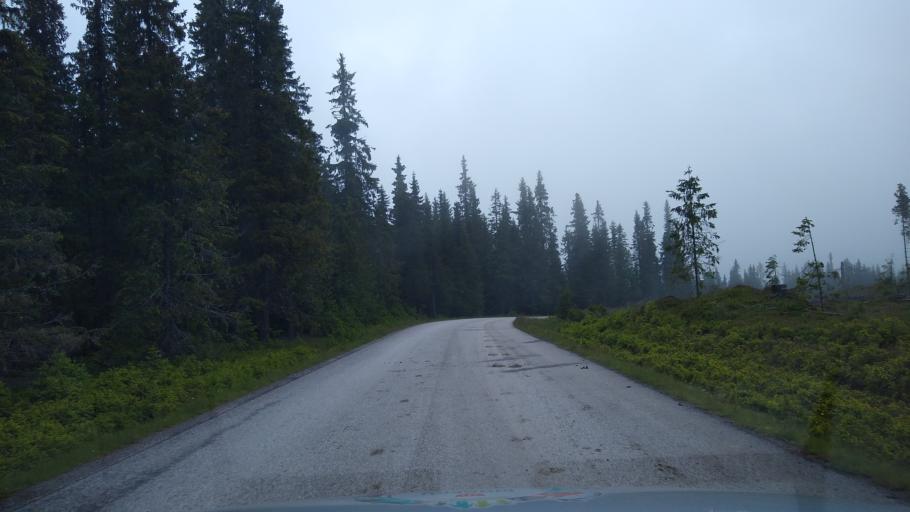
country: NO
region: Oppland
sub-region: Ringebu
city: Ringebu
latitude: 61.4924
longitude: 10.1259
